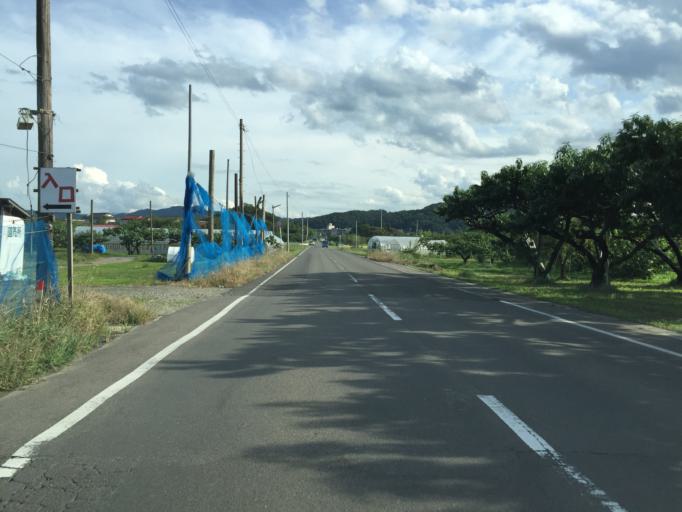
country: JP
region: Fukushima
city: Hobaramachi
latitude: 37.8194
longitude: 140.5383
